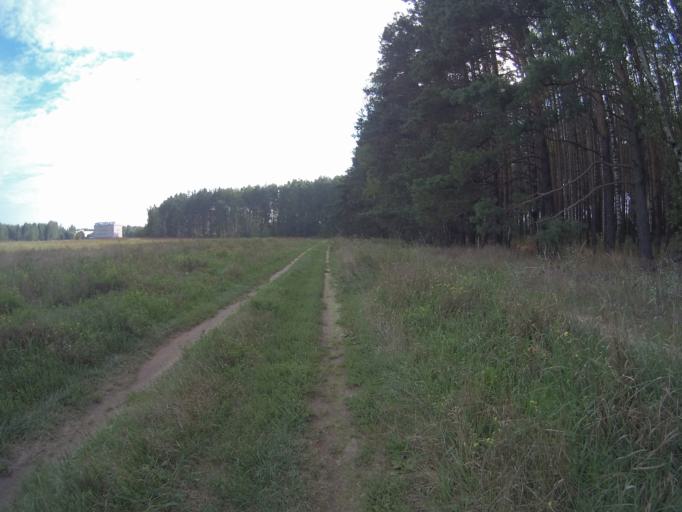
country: RU
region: Vladimir
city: Raduzhnyy
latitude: 56.0092
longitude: 40.2985
